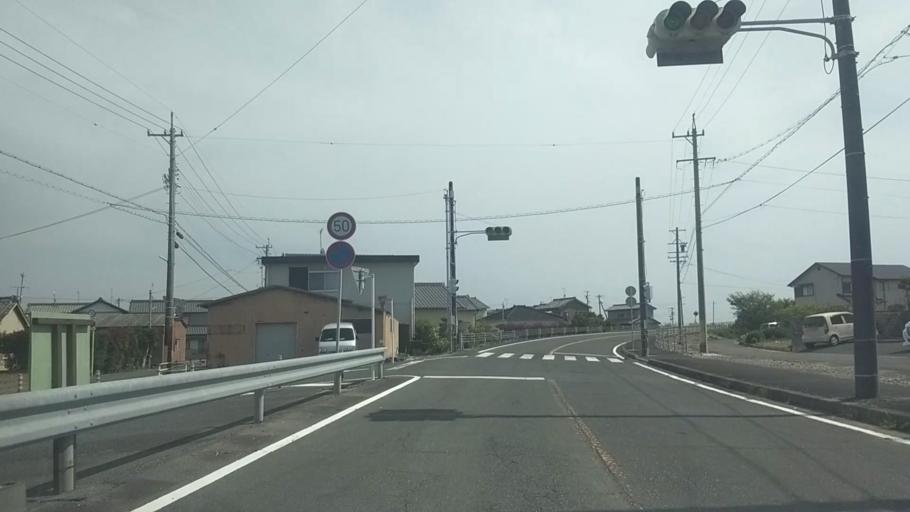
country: JP
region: Shizuoka
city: Kosai-shi
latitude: 34.7256
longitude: 137.5897
